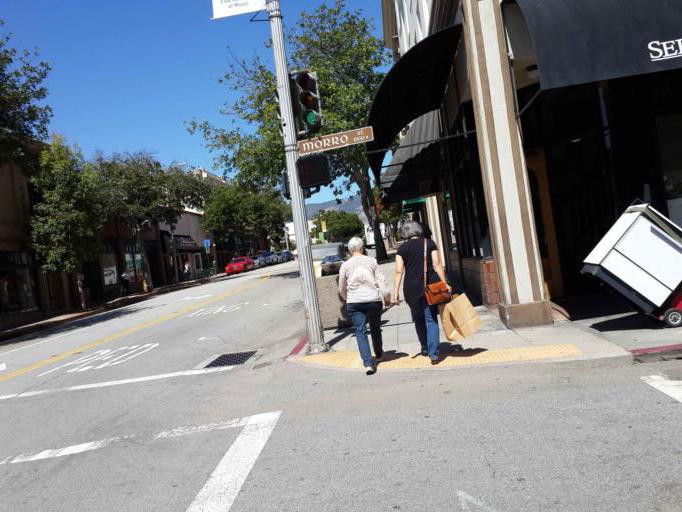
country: US
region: California
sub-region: San Luis Obispo County
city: San Luis Obispo
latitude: 35.2813
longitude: -120.6623
